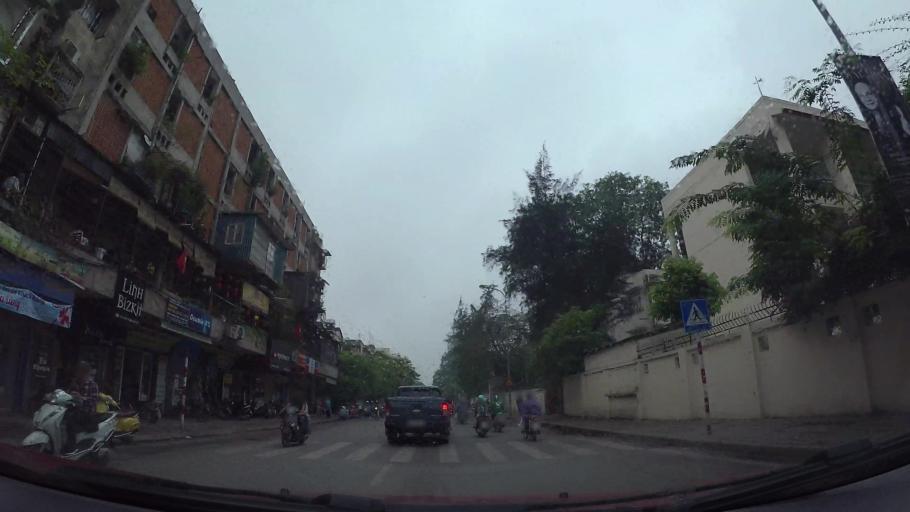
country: VN
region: Ha Noi
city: Dong Da
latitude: 21.0051
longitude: 105.8306
